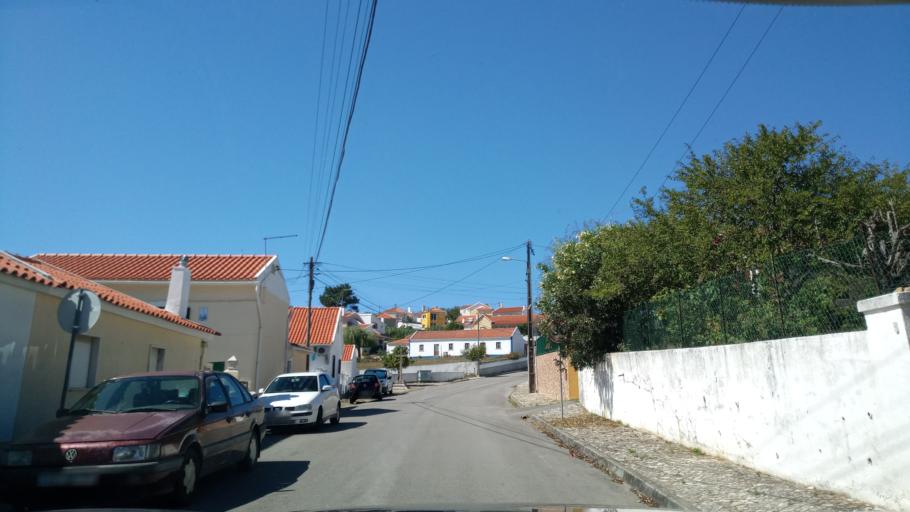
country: PT
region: Lisbon
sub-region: Mafra
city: Malveira
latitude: 38.9204
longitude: -9.2902
